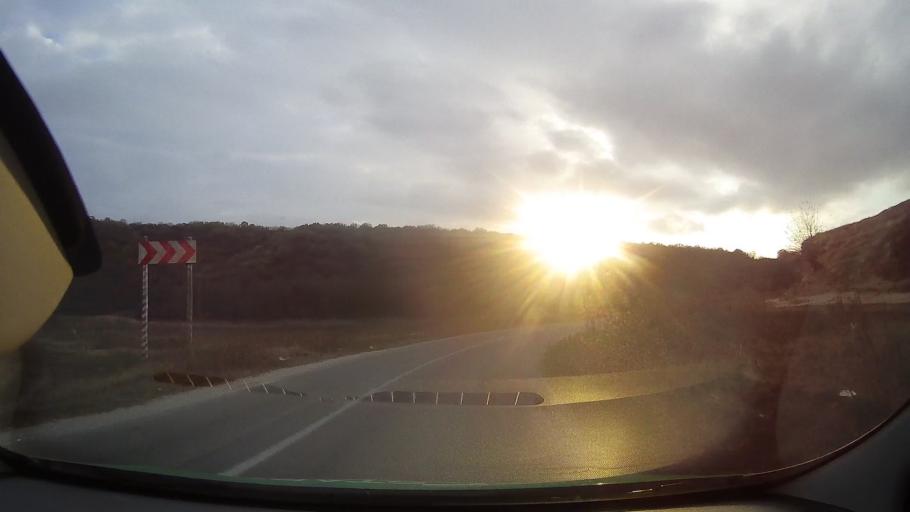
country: RO
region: Constanta
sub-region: Comuna Adamclisi
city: Adamclisi
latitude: 44.0389
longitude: 27.9512
